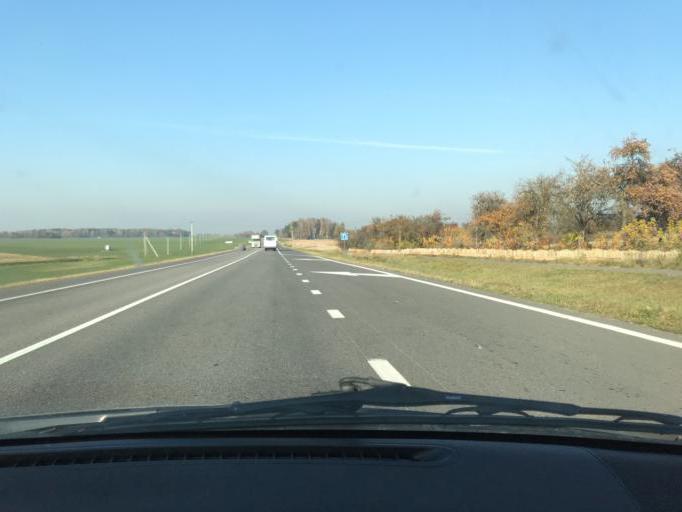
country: BY
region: Vitebsk
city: Balbasava
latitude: 54.3160
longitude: 30.4474
